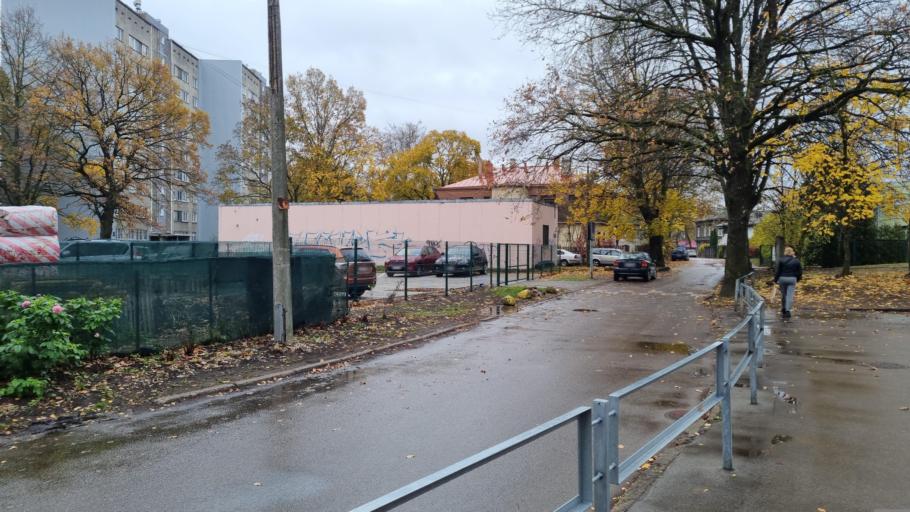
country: LV
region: Riga
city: Riga
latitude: 56.9626
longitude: 24.0525
